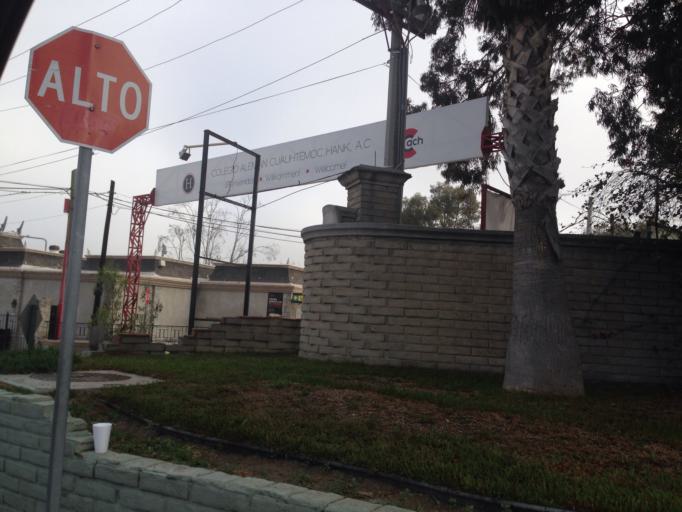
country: MX
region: Baja California
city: Tijuana
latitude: 32.5035
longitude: -116.9985
